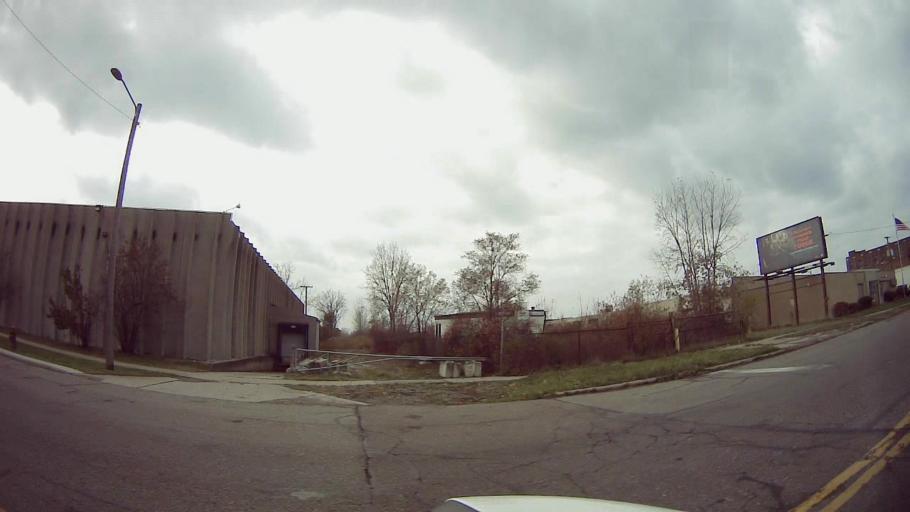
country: US
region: Michigan
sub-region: Wayne County
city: Highland Park
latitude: 42.3964
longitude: -83.1348
